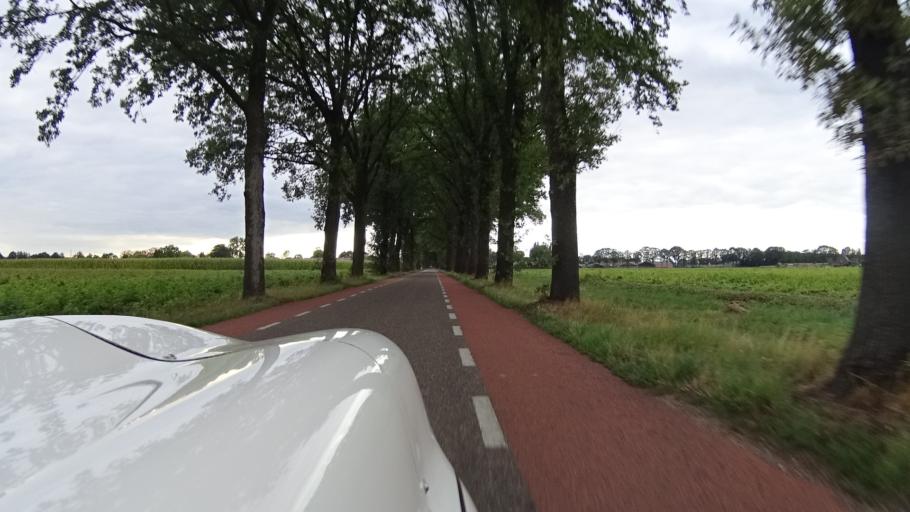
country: NL
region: North Brabant
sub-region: Gemeente Bernheze
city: Loosbroek
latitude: 51.6713
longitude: 5.5314
